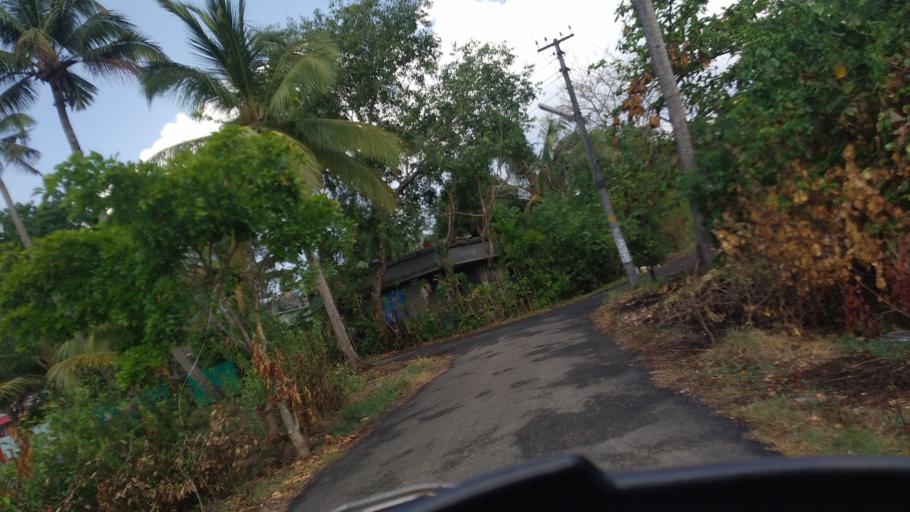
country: IN
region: Kerala
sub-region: Thrissur District
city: Kodungallur
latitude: 10.1362
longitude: 76.2128
